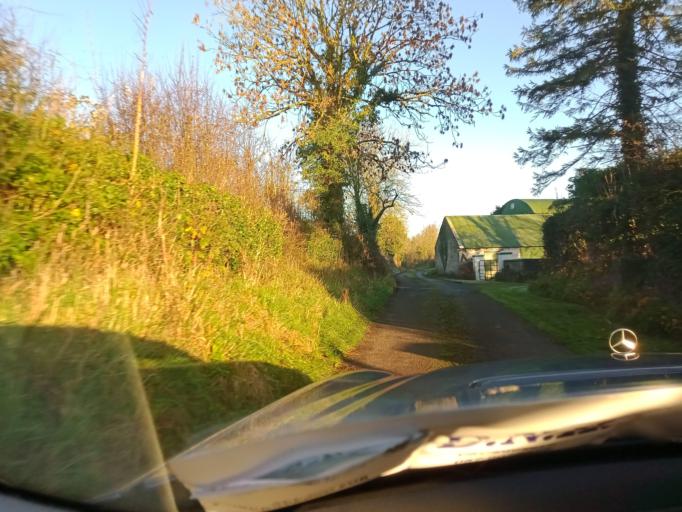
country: IE
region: Leinster
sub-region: Kilkenny
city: Callan
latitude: 52.5343
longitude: -7.4219
